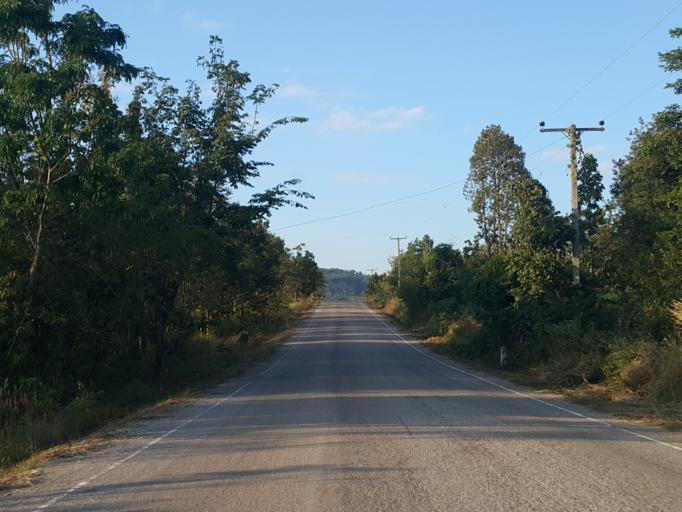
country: TH
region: Lampang
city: Lampang
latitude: 18.4329
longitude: 99.5710
